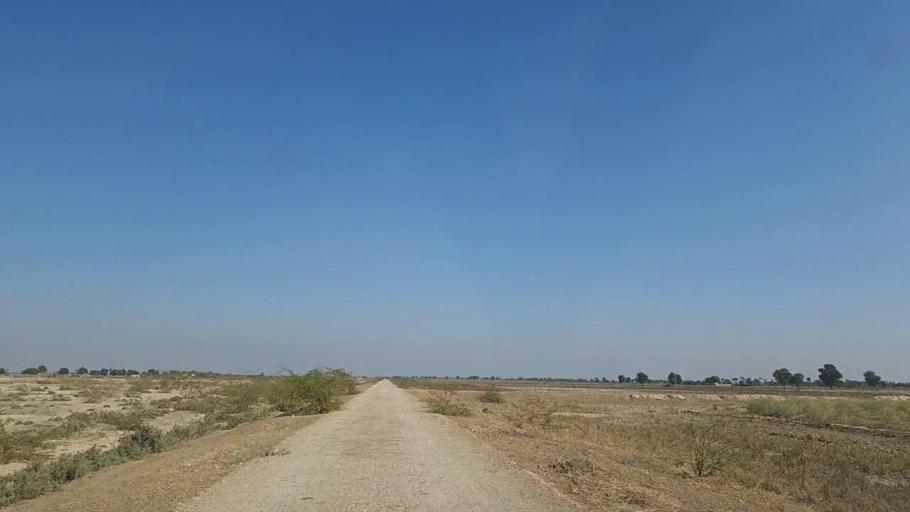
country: PK
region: Sindh
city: Samaro
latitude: 25.3991
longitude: 69.4159
